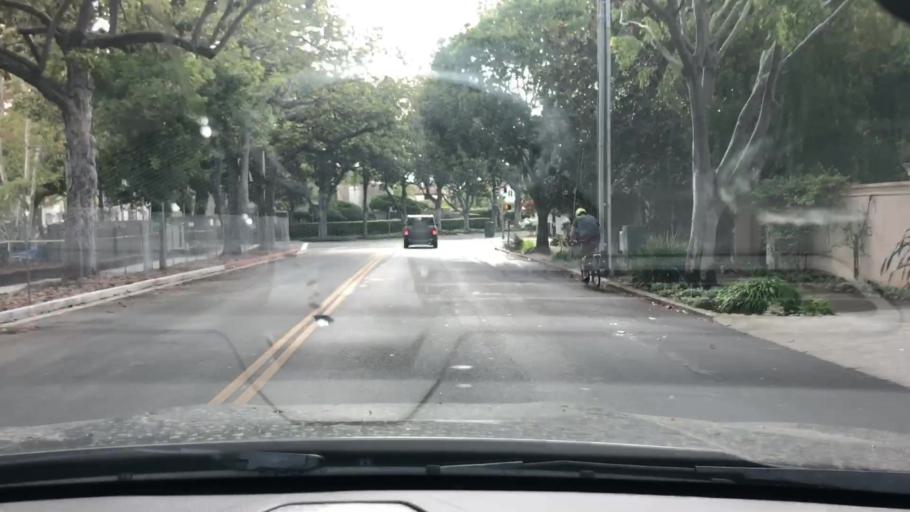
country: US
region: California
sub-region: Santa Clara County
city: Palo Alto
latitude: 37.4559
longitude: -122.1525
